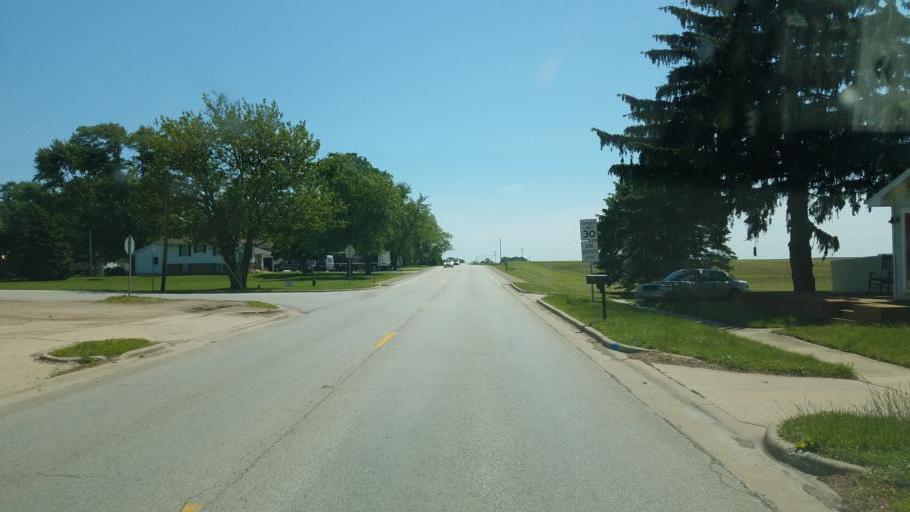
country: US
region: Illinois
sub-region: McLean County
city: Heyworth
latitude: 40.3120
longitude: -88.9729
